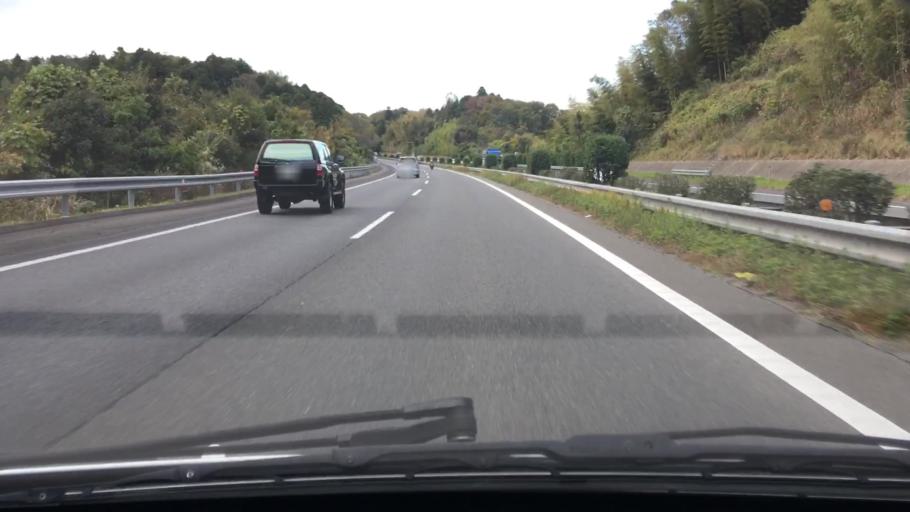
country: JP
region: Chiba
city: Ichihara
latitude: 35.4394
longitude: 140.0572
